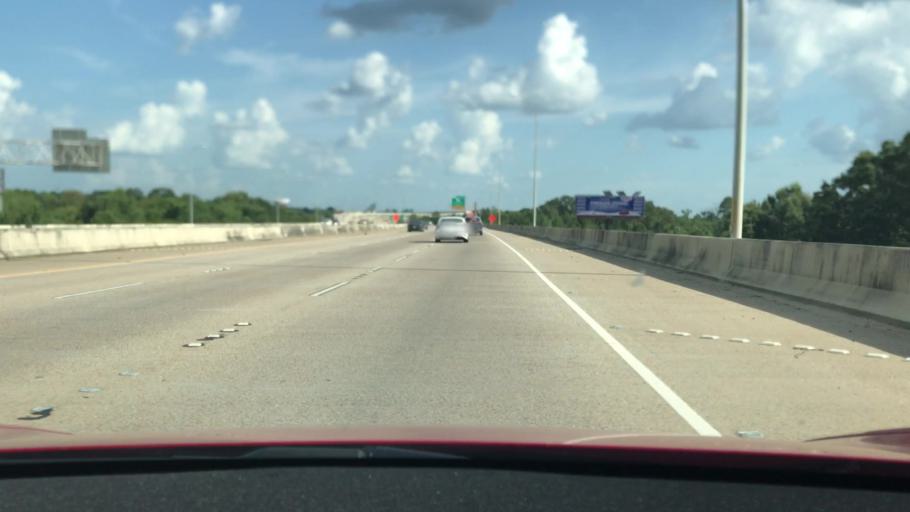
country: US
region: Louisiana
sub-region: Bossier Parish
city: Bossier City
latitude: 32.4322
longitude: -93.7547
